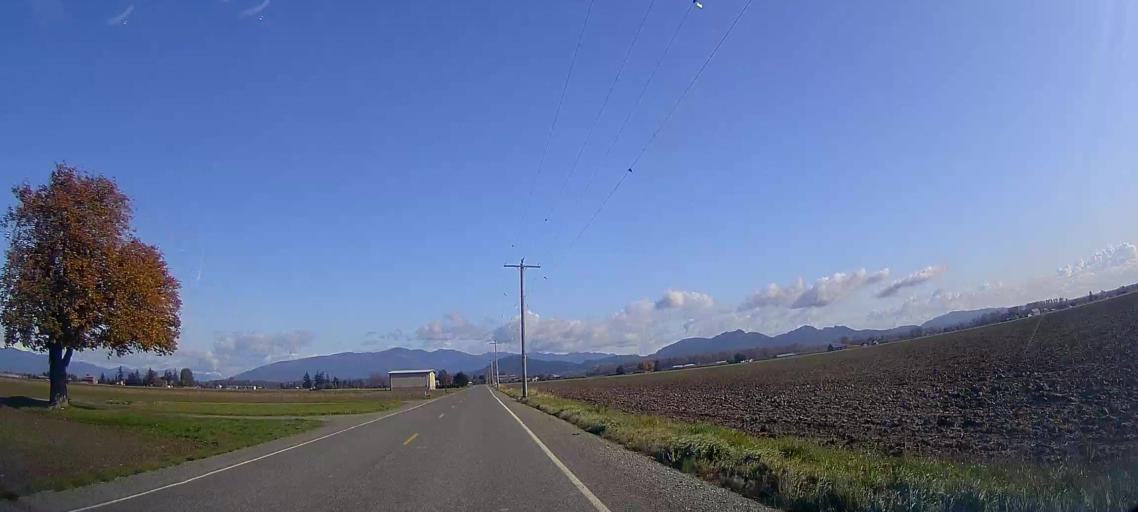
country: US
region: Washington
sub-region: Skagit County
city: Mount Vernon
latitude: 48.3992
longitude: -122.4120
